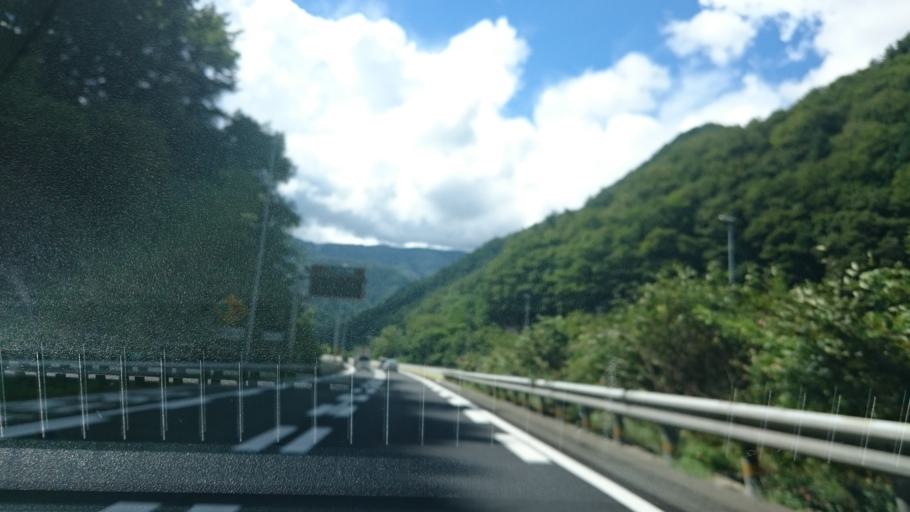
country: JP
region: Nagano
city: Iida
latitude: 35.4563
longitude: 137.6837
